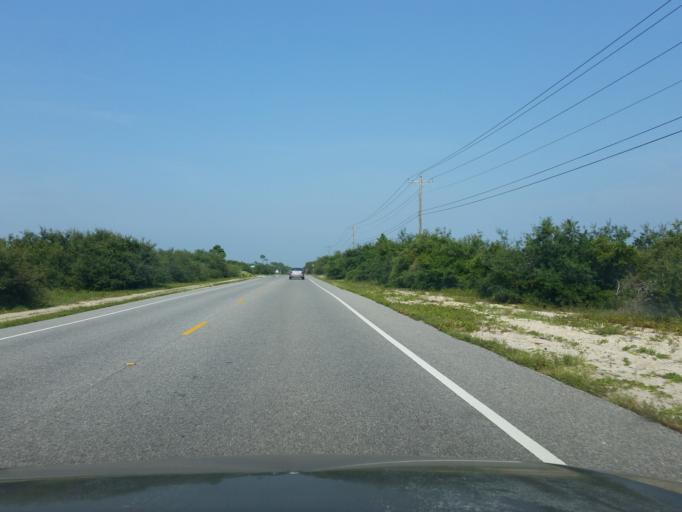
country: US
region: Alabama
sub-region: Mobile County
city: Dauphin Island
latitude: 30.2349
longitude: -87.9275
